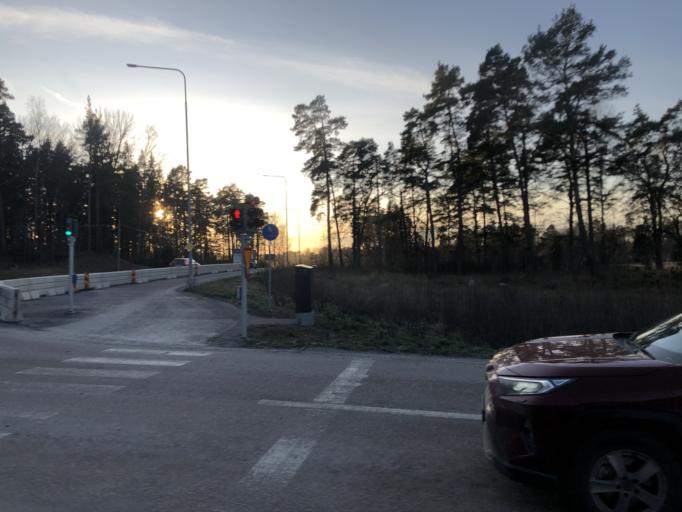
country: SE
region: Stockholm
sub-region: Jarfalla Kommun
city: Jakobsberg
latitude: 59.4098
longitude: 17.8853
